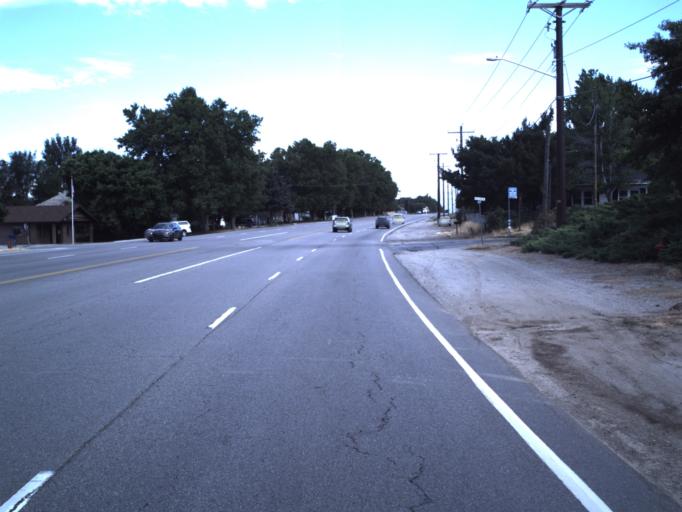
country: US
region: Utah
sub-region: Box Elder County
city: Willard
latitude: 41.4047
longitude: -112.0362
